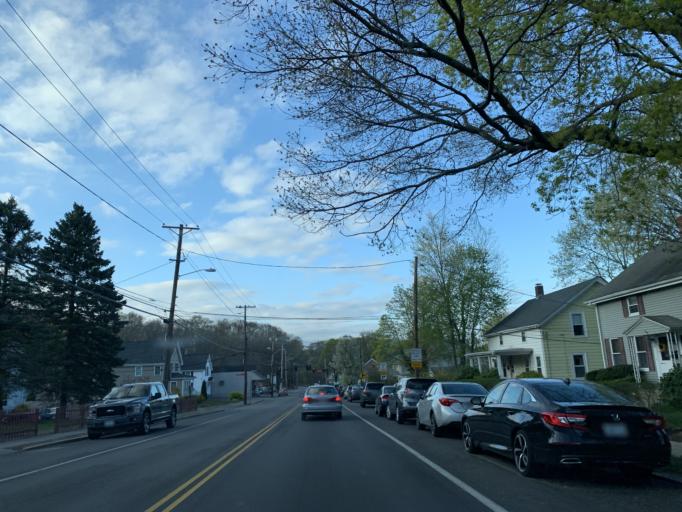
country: US
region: Rhode Island
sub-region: Providence County
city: Central Falls
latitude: 41.8910
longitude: -71.4118
